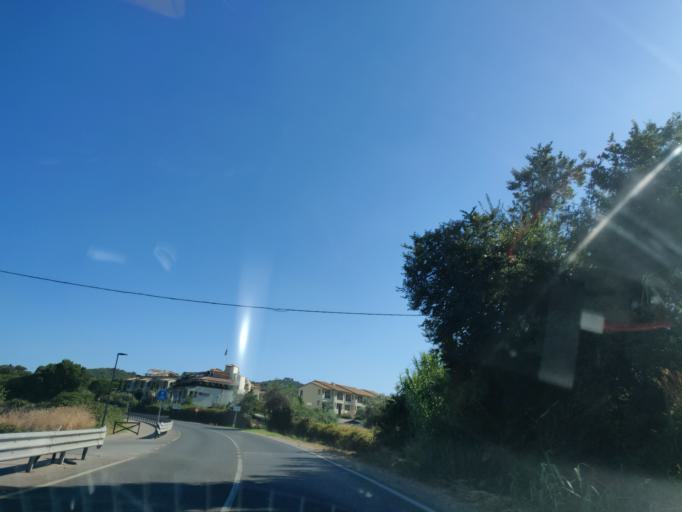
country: IT
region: Tuscany
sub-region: Provincia di Grosseto
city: Porto Ercole
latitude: 42.4018
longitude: 11.1994
